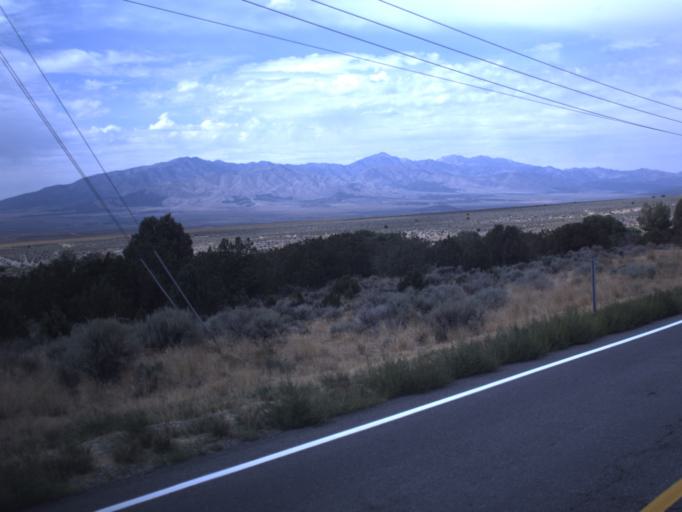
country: US
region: Utah
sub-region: Tooele County
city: Tooele
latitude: 40.3382
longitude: -112.3009
